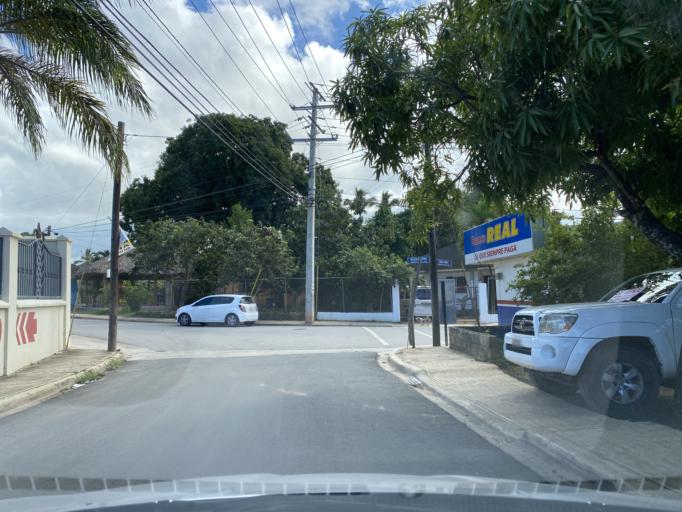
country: DO
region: Samana
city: Las Terrenas
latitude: 19.3080
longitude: -69.5516
